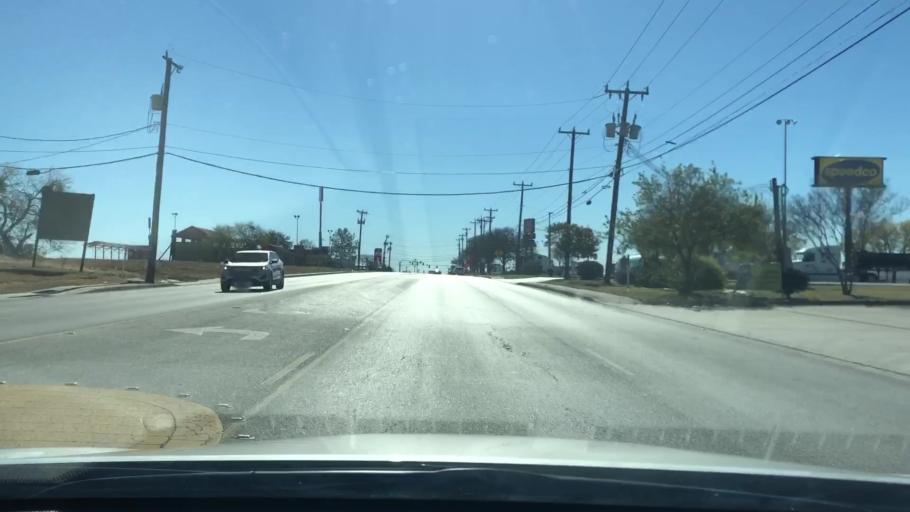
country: US
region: Texas
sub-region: Bexar County
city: Kirby
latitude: 29.4489
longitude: -98.3608
